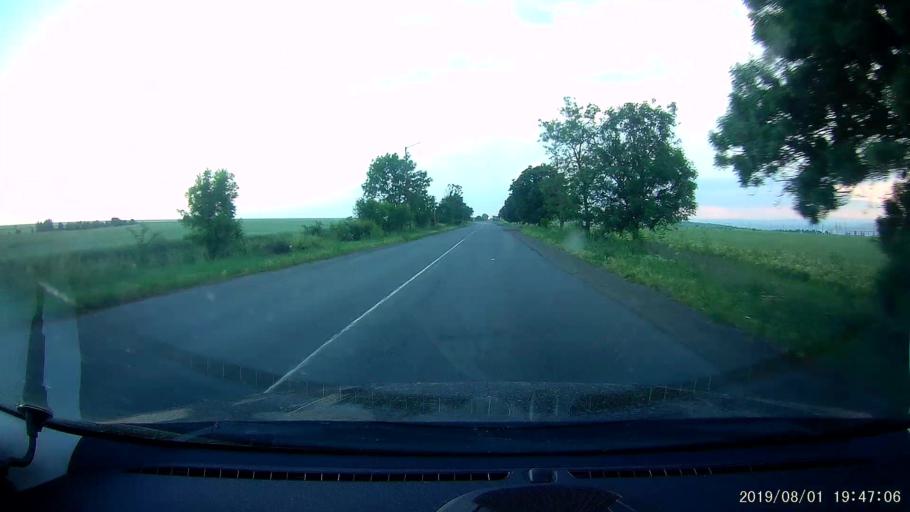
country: BG
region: Burgas
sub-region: Obshtina Karnobat
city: Karnobat
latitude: 42.6507
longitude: 26.9620
